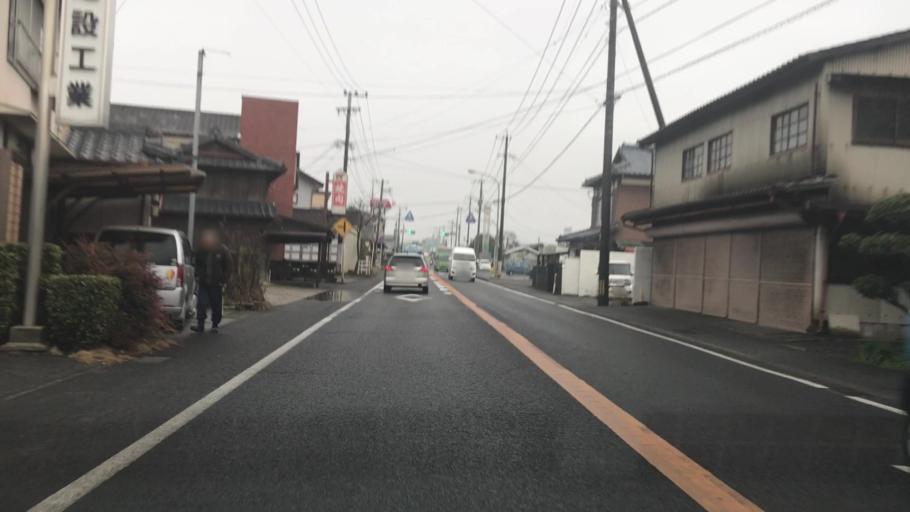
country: JP
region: Saga Prefecture
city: Takeocho-takeo
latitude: 33.2129
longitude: 130.1046
